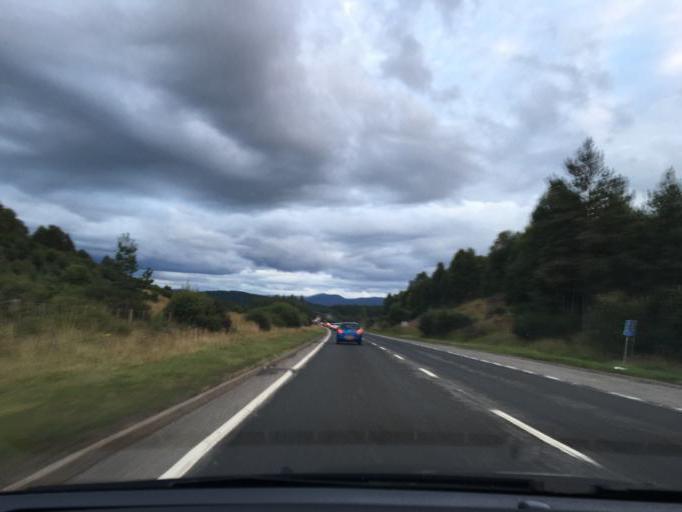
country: GB
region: Scotland
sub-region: Highland
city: Aviemore
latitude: 57.2844
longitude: -3.8393
